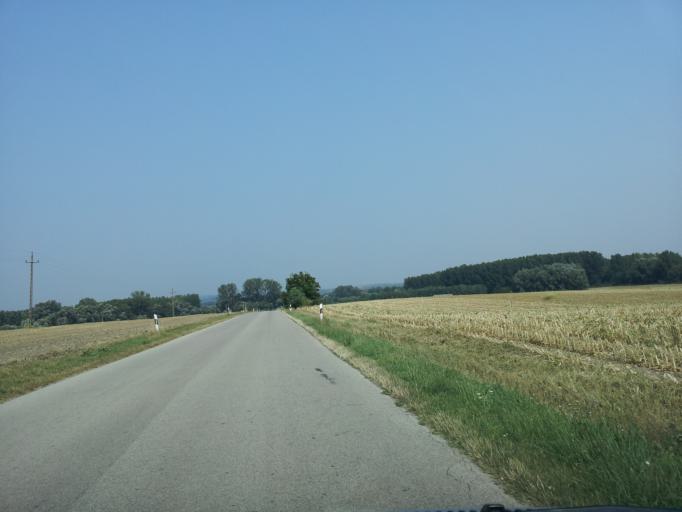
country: HU
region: Gyor-Moson-Sopron
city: Bakonyszentlaszlo
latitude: 47.4019
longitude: 17.8006
